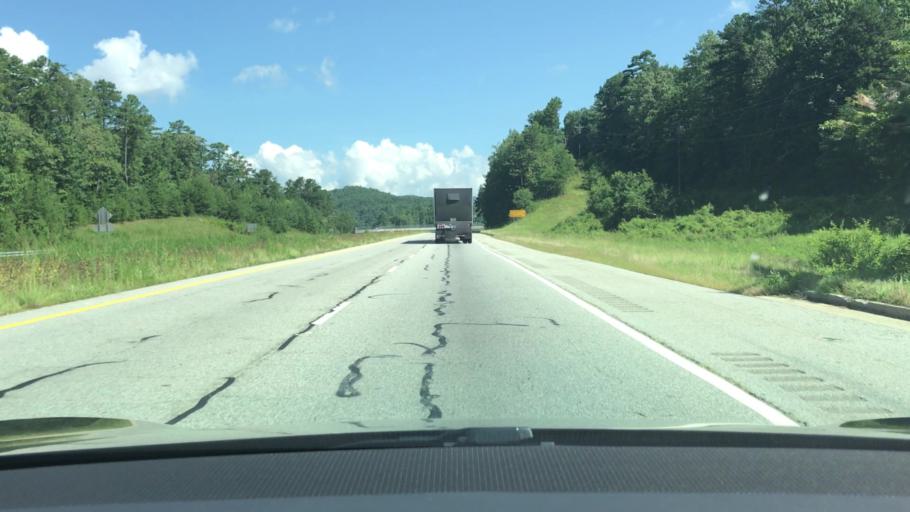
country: US
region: Georgia
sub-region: Rabun County
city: Clayton
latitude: 34.8225
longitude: -83.4237
